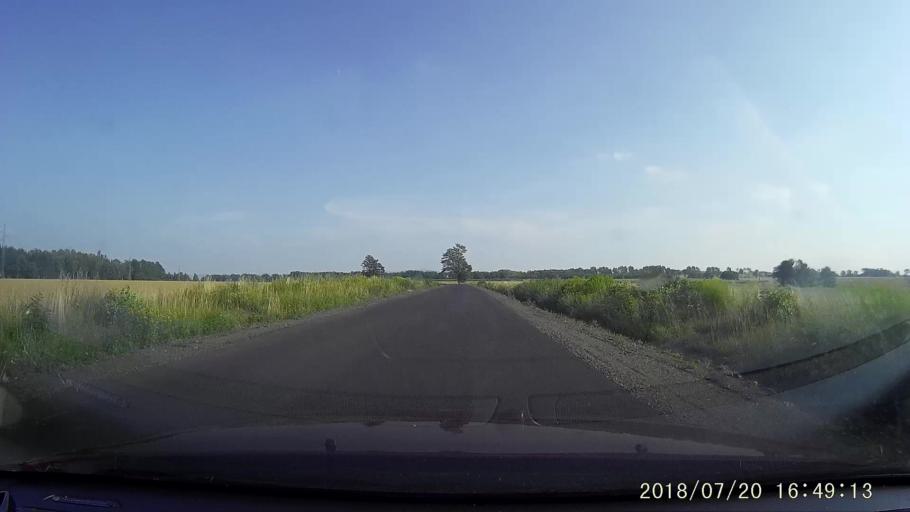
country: PL
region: Lower Silesian Voivodeship
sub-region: Powiat lubanski
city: Siekierczyn
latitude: 51.0498
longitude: 15.1948
